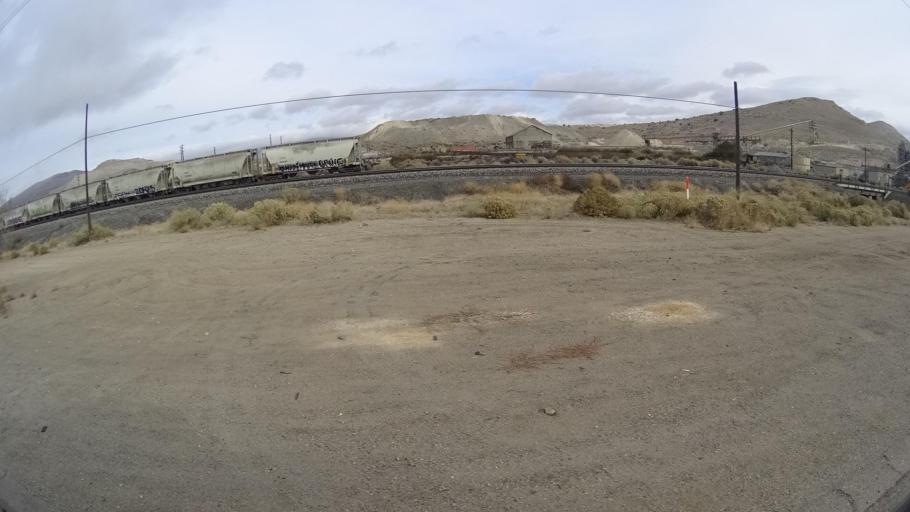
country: US
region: California
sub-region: Kern County
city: Tehachapi
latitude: 35.1220
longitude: -118.3739
